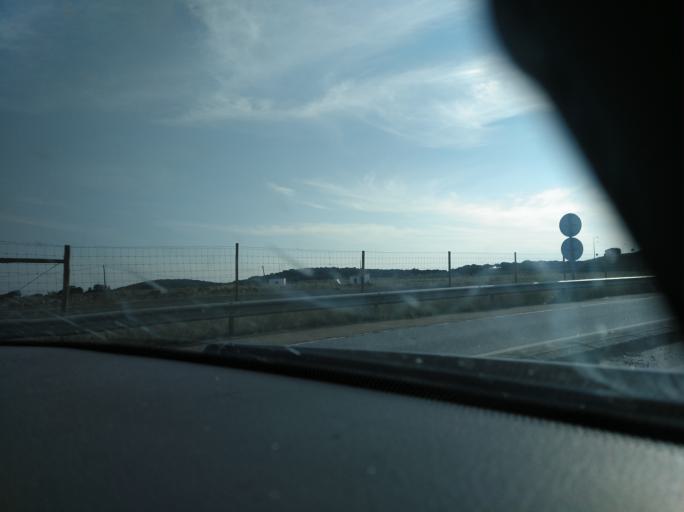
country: PT
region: Portalegre
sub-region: Elvas
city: Elvas
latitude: 38.8664
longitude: -7.2185
